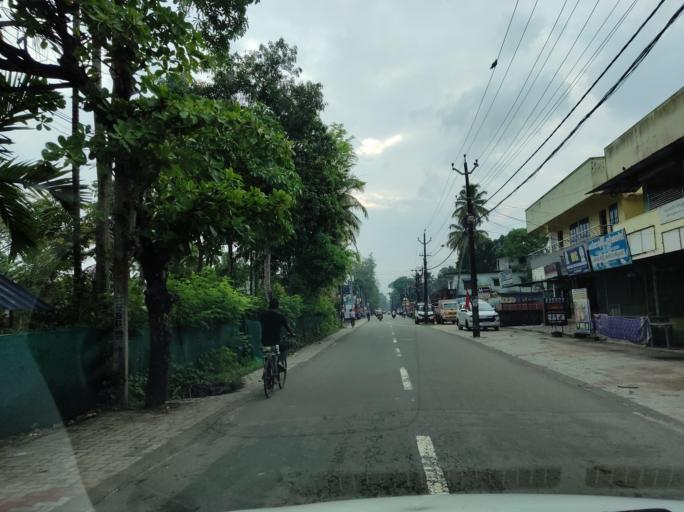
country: IN
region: Kerala
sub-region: Alappuzha
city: Kayankulam
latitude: 9.2592
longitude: 76.4366
